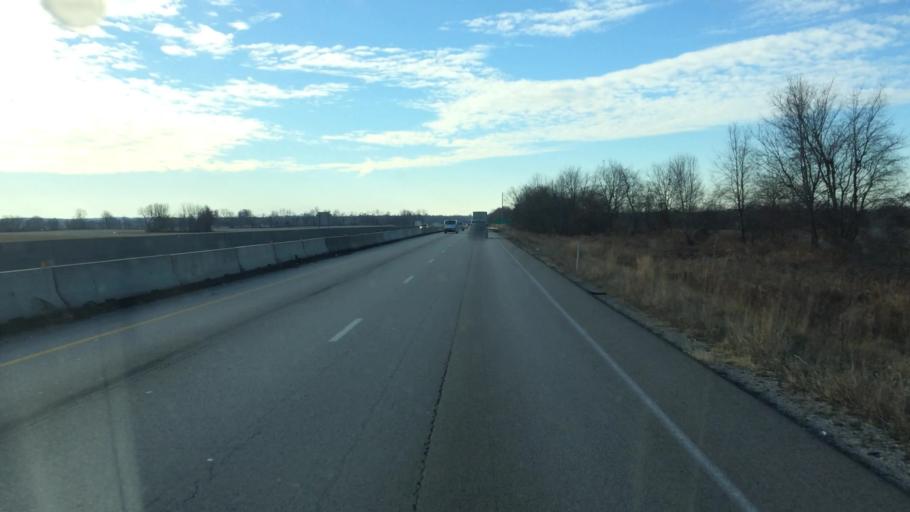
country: US
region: Kentucky
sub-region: Hardin County
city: Elizabethtown
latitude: 37.5849
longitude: -85.8714
